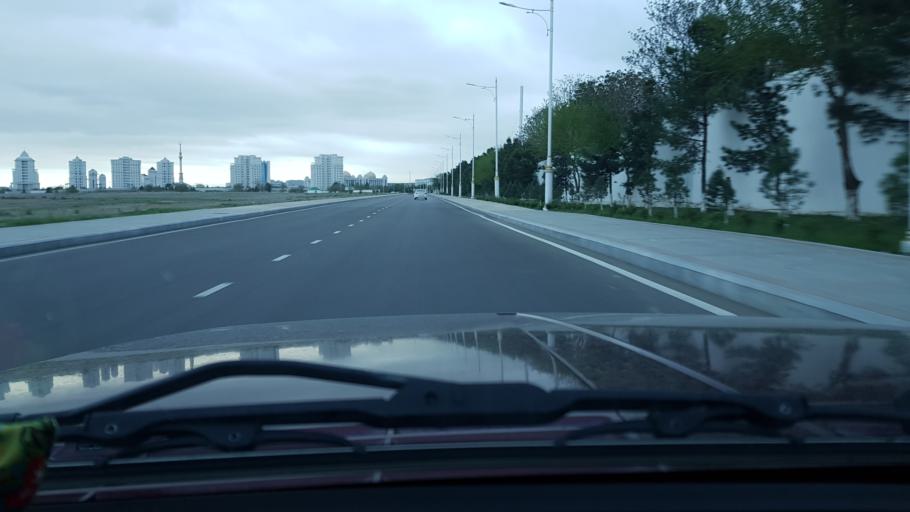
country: TM
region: Ahal
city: Ashgabat
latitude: 37.8857
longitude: 58.3614
